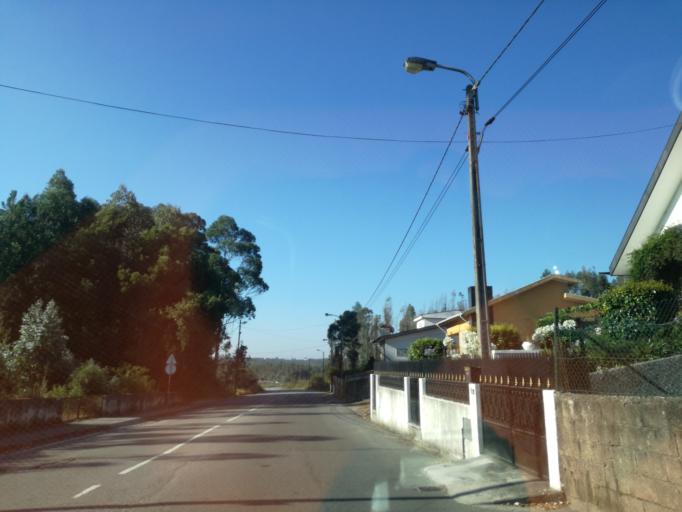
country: PT
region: Porto
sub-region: Maia
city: Nogueira
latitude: 41.2598
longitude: -8.5738
